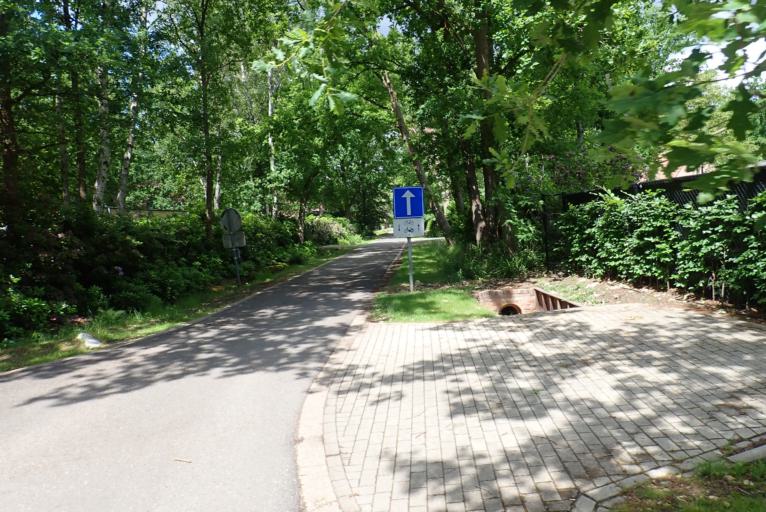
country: BE
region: Flanders
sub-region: Provincie Antwerpen
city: Schilde
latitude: 51.2589
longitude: 4.6028
